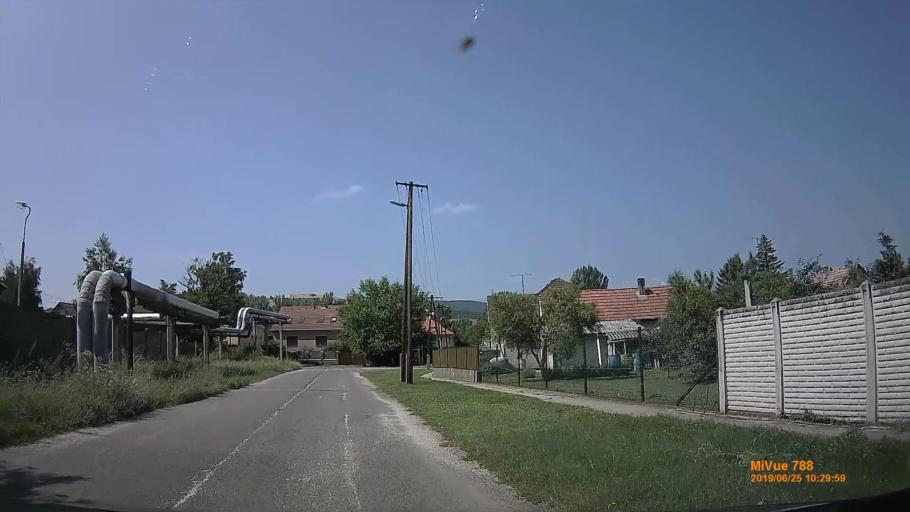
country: HU
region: Komarom-Esztergom
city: Dorog
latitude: 47.7322
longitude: 18.7230
